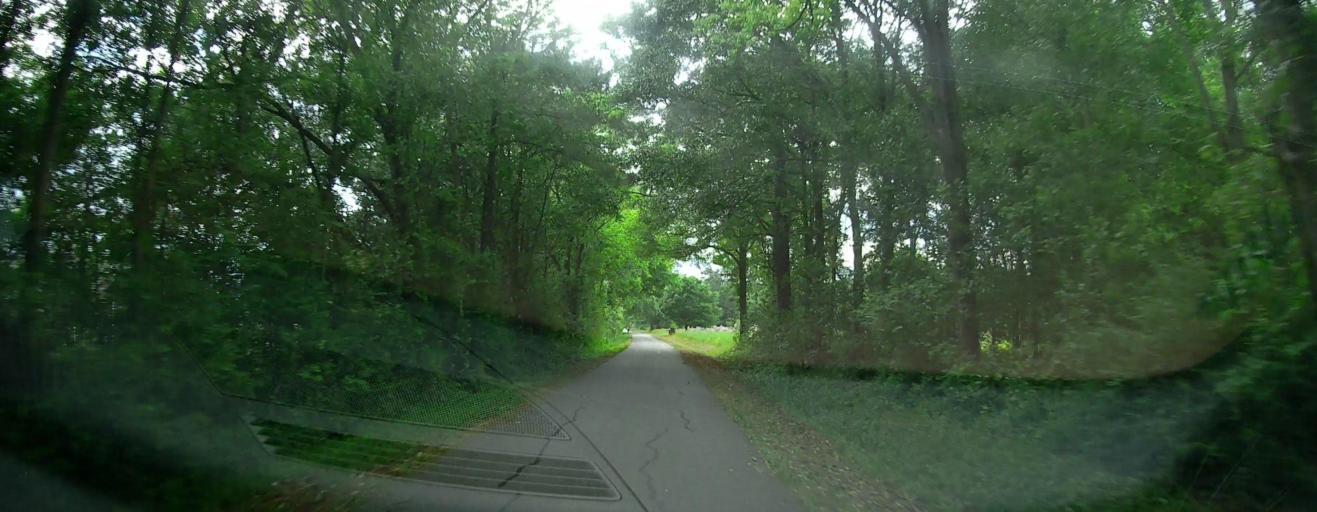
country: US
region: Georgia
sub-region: Oconee County
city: Watkinsville
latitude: 33.8210
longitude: -83.4420
